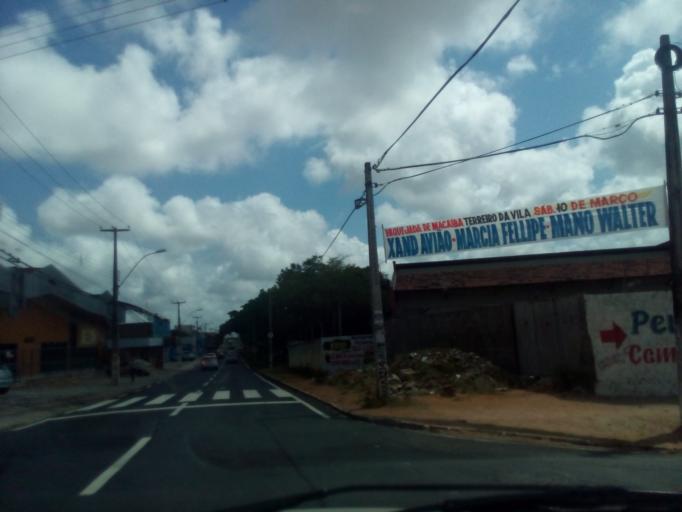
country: BR
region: Rio Grande do Norte
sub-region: Natal
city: Natal
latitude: -5.8555
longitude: -35.2058
